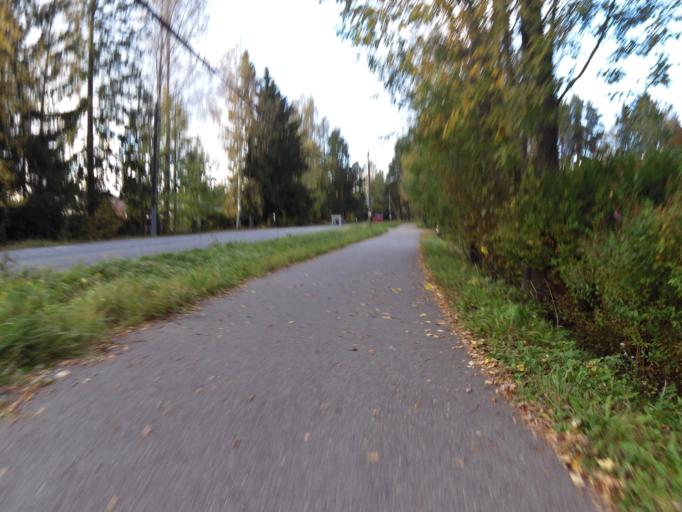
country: FI
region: Uusimaa
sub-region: Helsinki
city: Kilo
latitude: 60.2803
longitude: 24.7487
